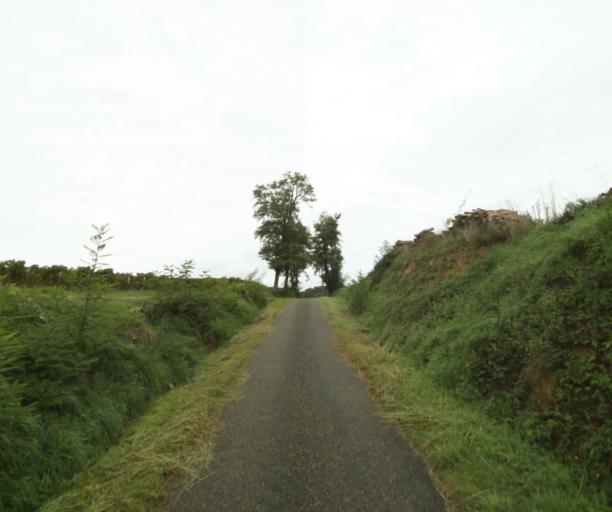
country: FR
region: Midi-Pyrenees
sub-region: Departement du Gers
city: Cazaubon
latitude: 43.8696
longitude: -0.0543
